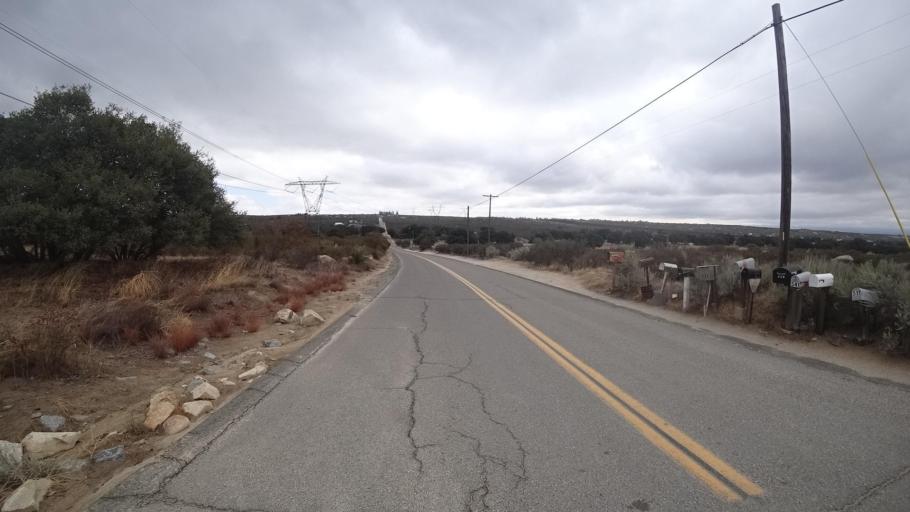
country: US
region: California
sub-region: San Diego County
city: Campo
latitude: 32.6044
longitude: -116.3510
